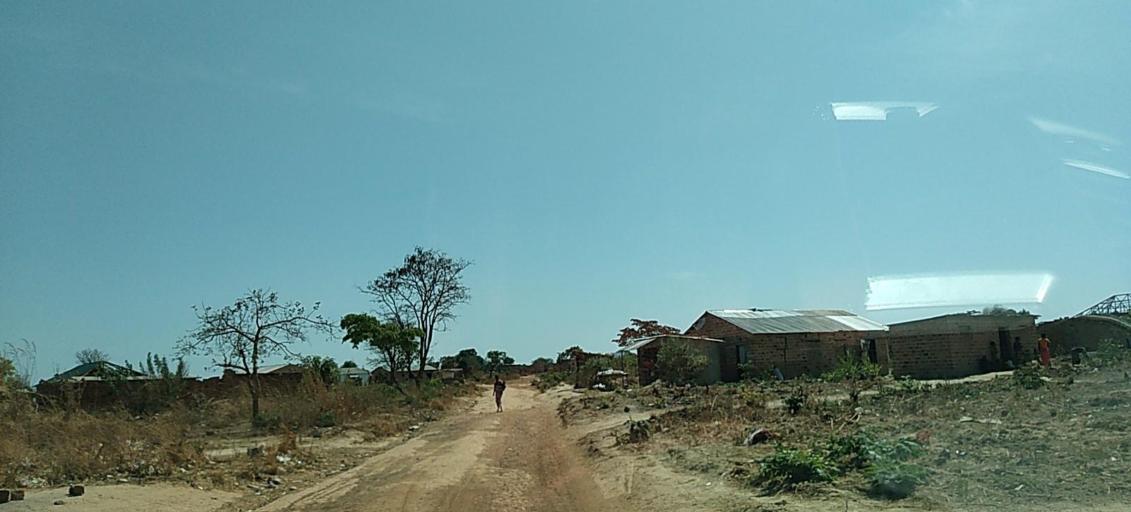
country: ZM
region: Copperbelt
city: Chililabombwe
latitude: -12.3207
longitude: 27.8606
